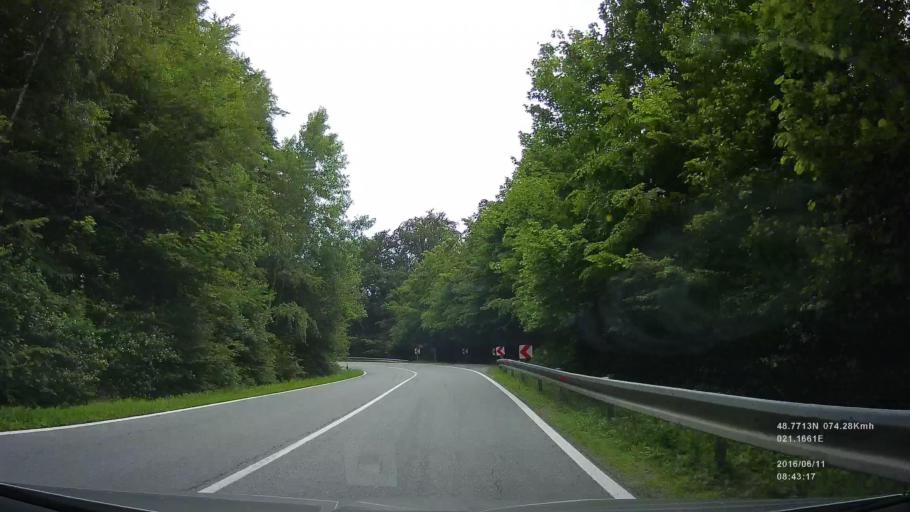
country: SK
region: Kosicky
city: Kosice
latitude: 48.7530
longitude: 21.2145
